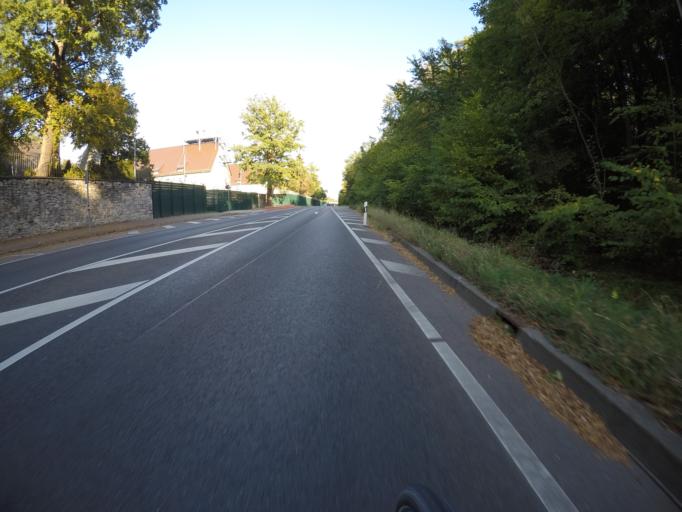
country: DE
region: Baden-Wuerttemberg
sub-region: Regierungsbezirk Stuttgart
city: Leinfelden-Echterdingen
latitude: 48.7215
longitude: 9.1754
